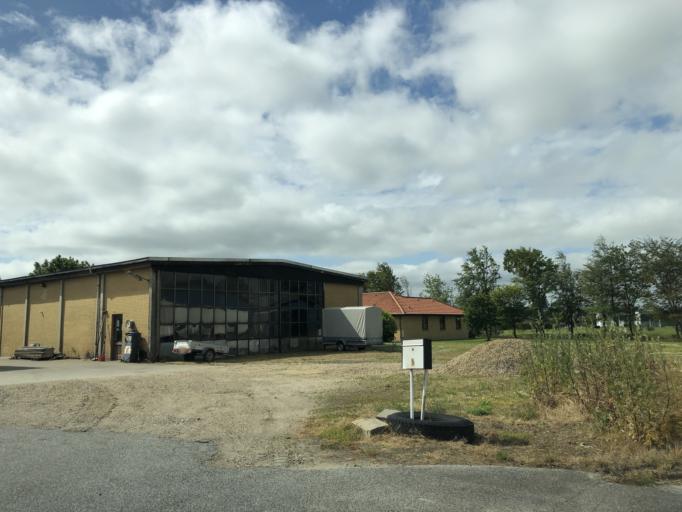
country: DK
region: Central Jutland
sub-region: Herning Kommune
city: Vildbjerg
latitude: 56.1921
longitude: 8.7550
